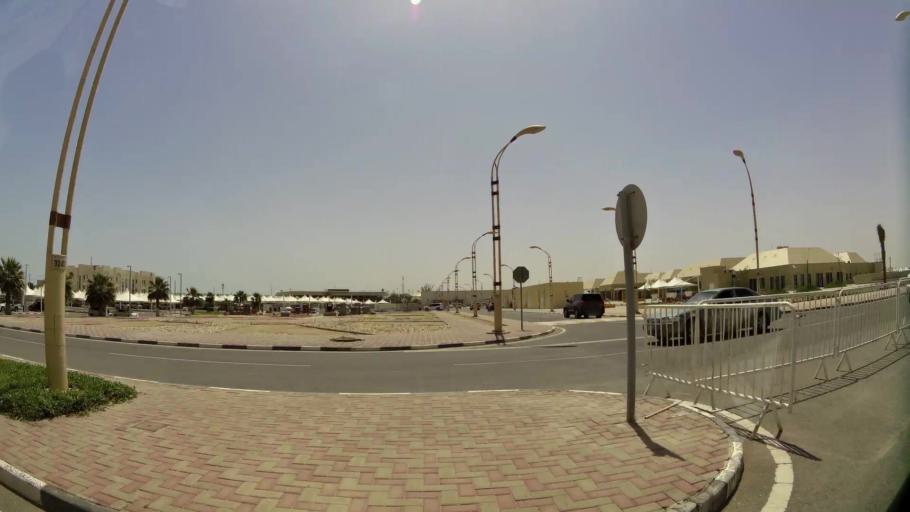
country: QA
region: Baladiyat Umm Salal
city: Umm Salal Muhammad
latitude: 25.3753
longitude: 51.4843
